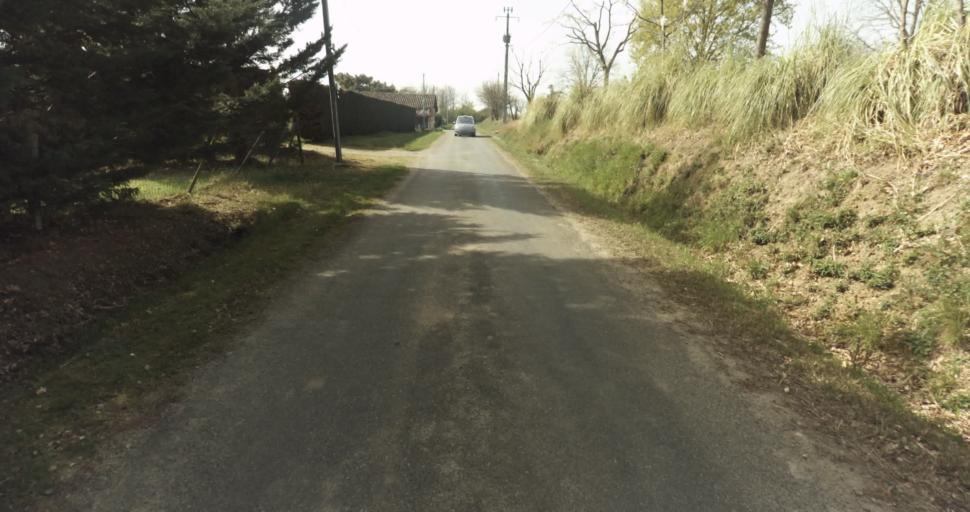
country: FR
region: Midi-Pyrenees
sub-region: Departement du Tarn-et-Garonne
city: Moissac
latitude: 44.1434
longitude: 1.1479
